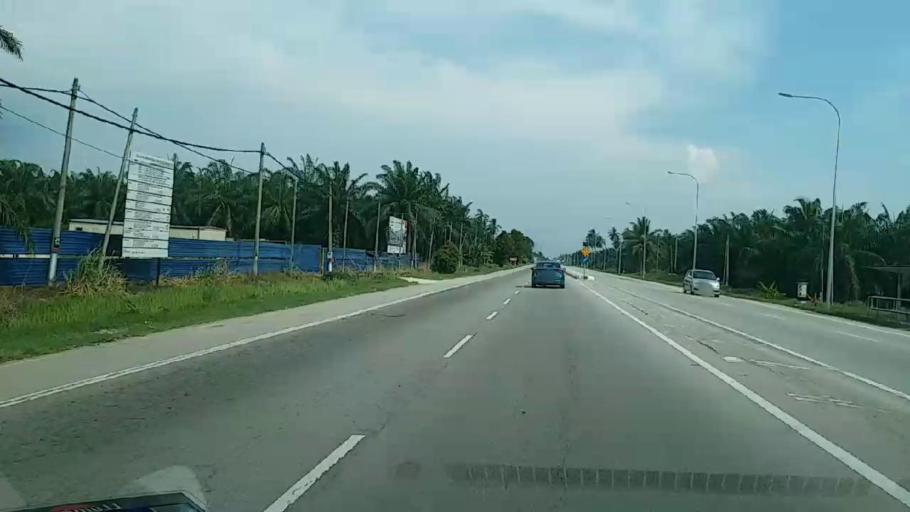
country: MY
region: Selangor
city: Kuala Selangor
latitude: 3.3776
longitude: 101.2358
